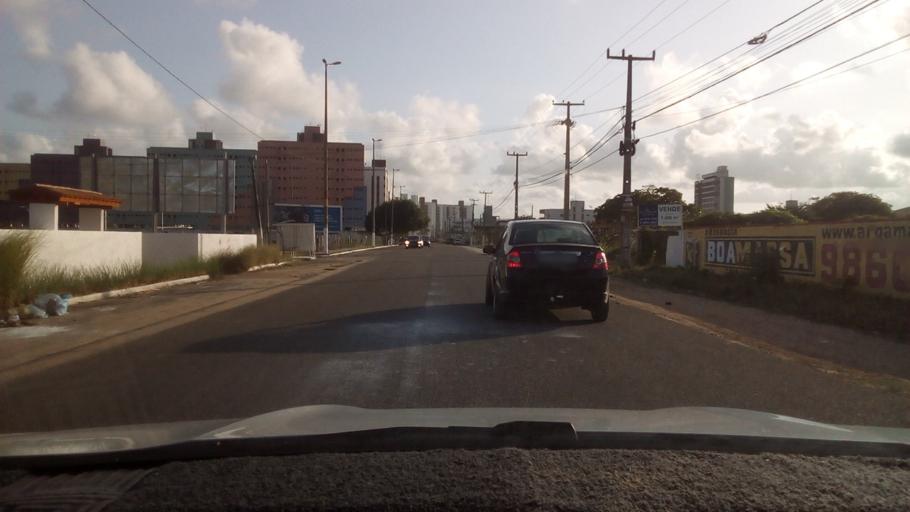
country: BR
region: Paraiba
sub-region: Cabedelo
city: Cabedelo
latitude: -7.0280
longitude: -34.8318
